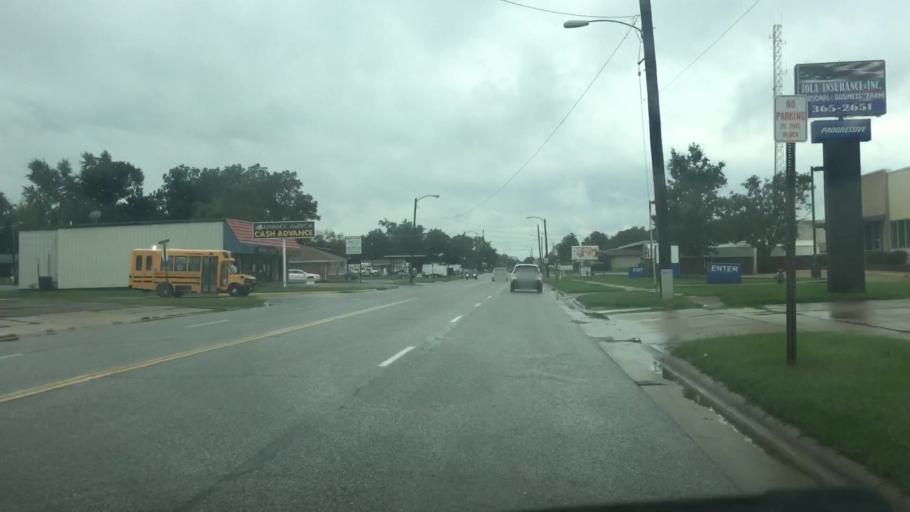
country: US
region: Kansas
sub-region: Allen County
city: Iola
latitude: 37.9281
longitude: -95.4091
